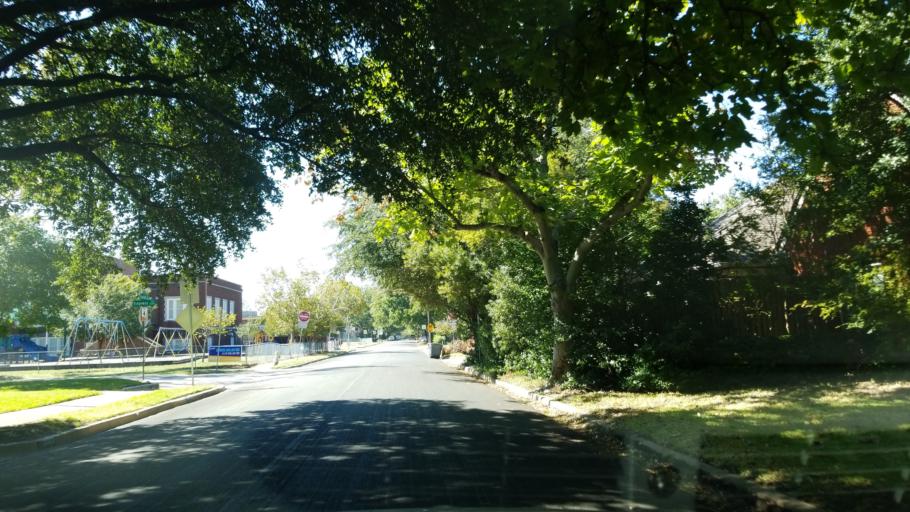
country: US
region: Texas
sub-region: Dallas County
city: Highland Park
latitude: 32.8083
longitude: -96.7565
